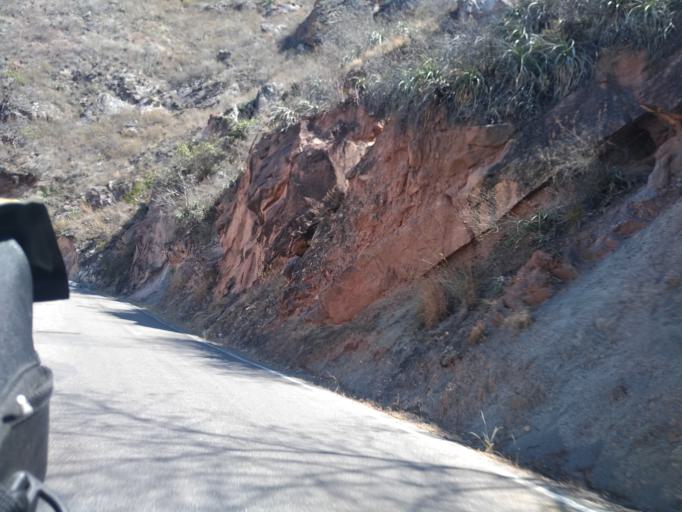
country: PE
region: Amazonas
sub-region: Provincia de Chachapoyas
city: Balsas
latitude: -6.8500
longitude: -77.9819
